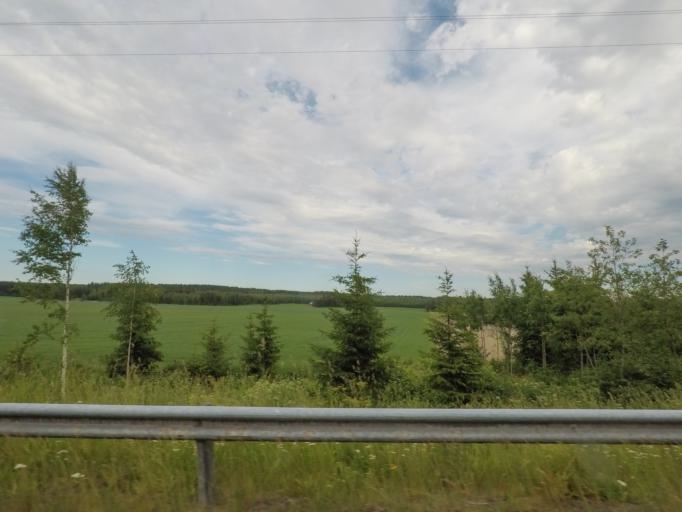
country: FI
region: Paijanne Tavastia
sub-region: Lahti
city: Hollola
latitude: 60.8536
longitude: 25.4982
